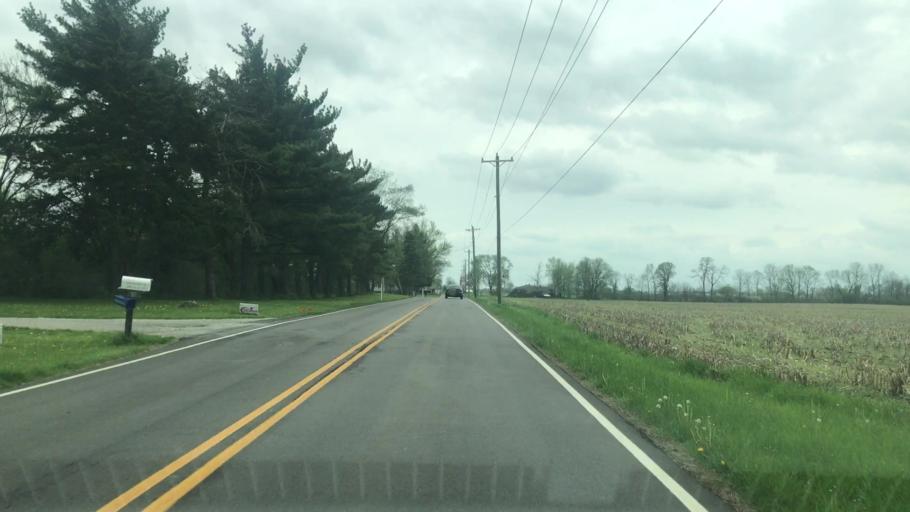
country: US
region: Indiana
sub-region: Johnson County
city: New Whiteland
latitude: 39.5791
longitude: -86.0829
